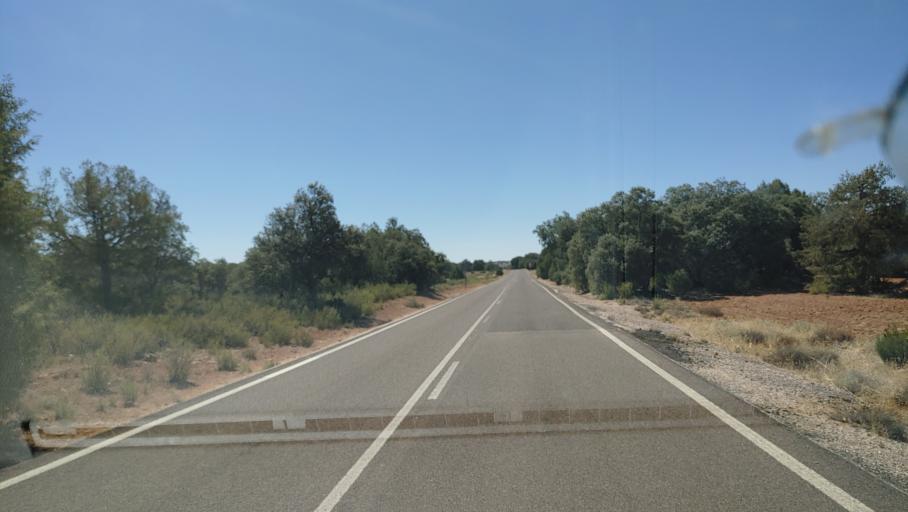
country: ES
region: Castille-La Mancha
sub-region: Provincia de Albacete
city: Ossa de Montiel
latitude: 38.8801
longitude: -2.7794
